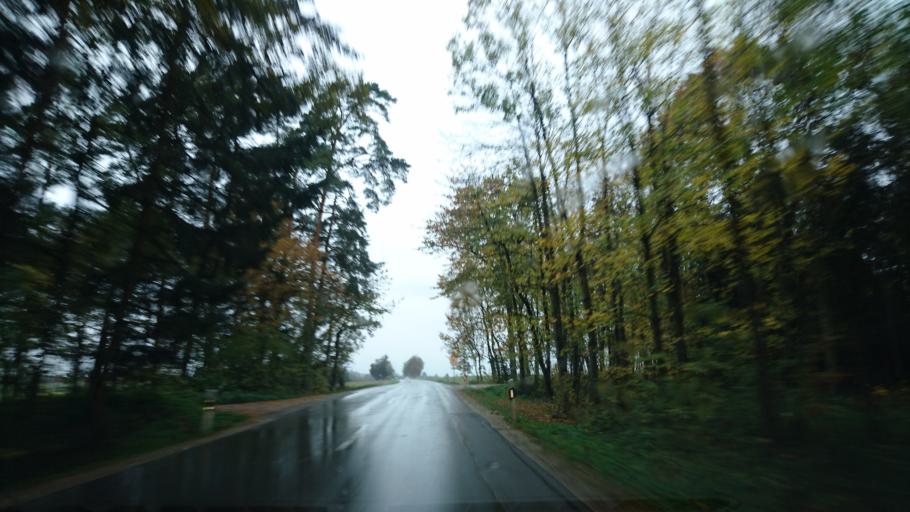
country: DE
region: Bavaria
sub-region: Upper Bavaria
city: Jetzendorf
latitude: 48.4238
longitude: 11.4352
